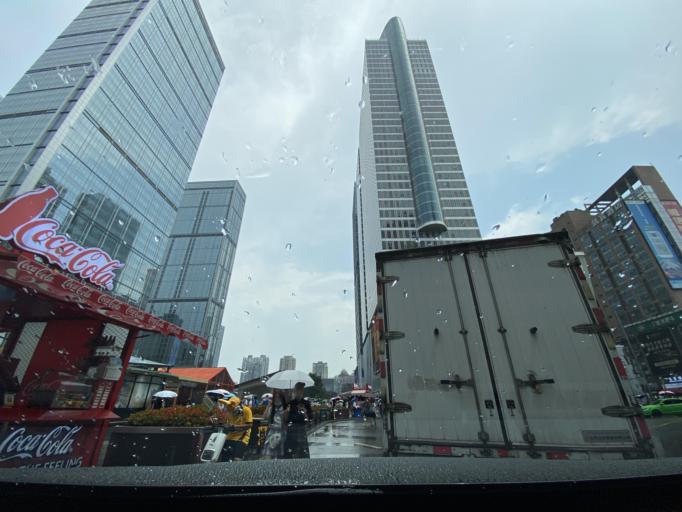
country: CN
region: Sichuan
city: Chengdu
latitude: 30.6563
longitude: 104.0766
